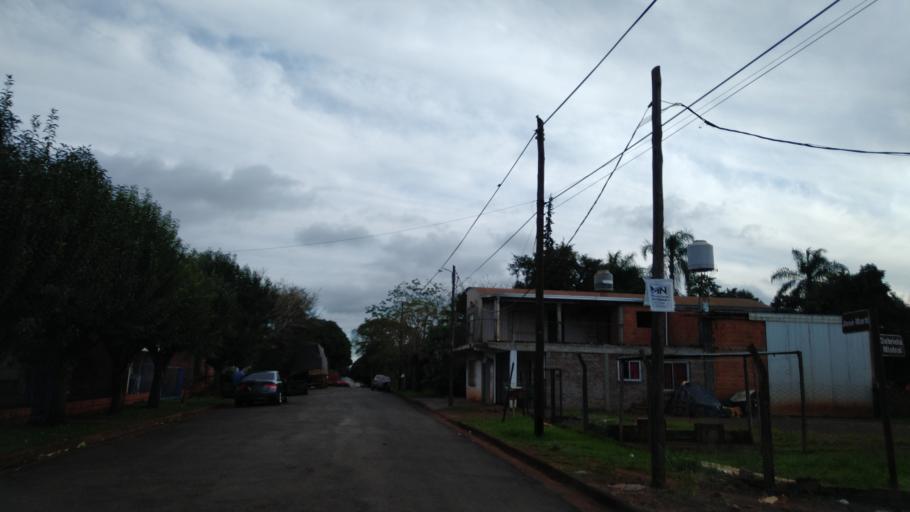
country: AR
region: Misiones
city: Jardin America
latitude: -27.0443
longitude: -55.2410
